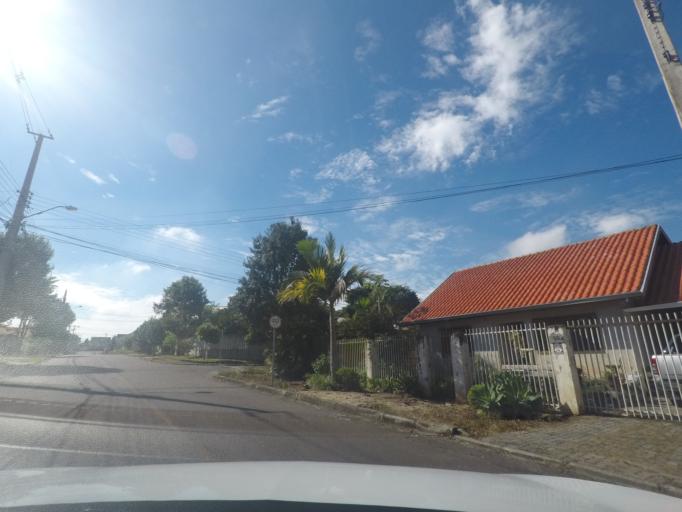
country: BR
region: Parana
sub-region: Sao Jose Dos Pinhais
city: Sao Jose dos Pinhais
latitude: -25.5103
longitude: -49.2584
